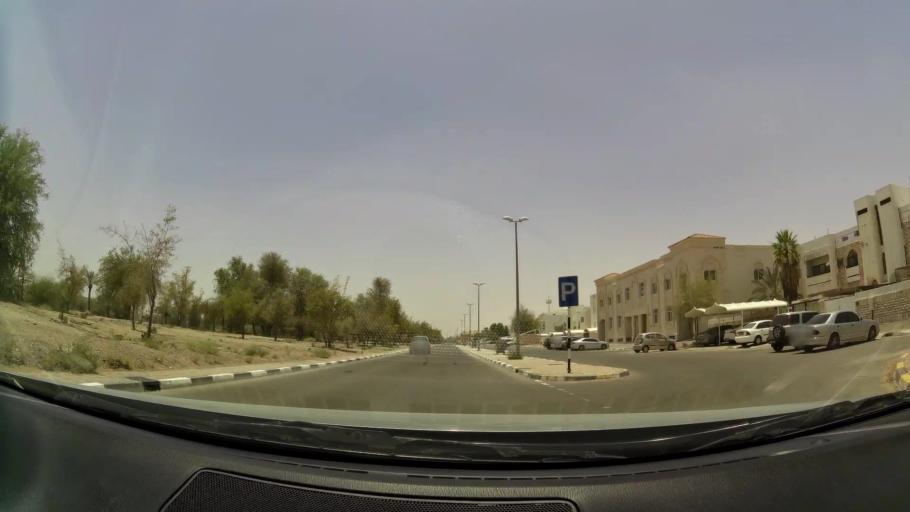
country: OM
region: Al Buraimi
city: Al Buraymi
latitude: 24.2596
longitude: 55.7266
